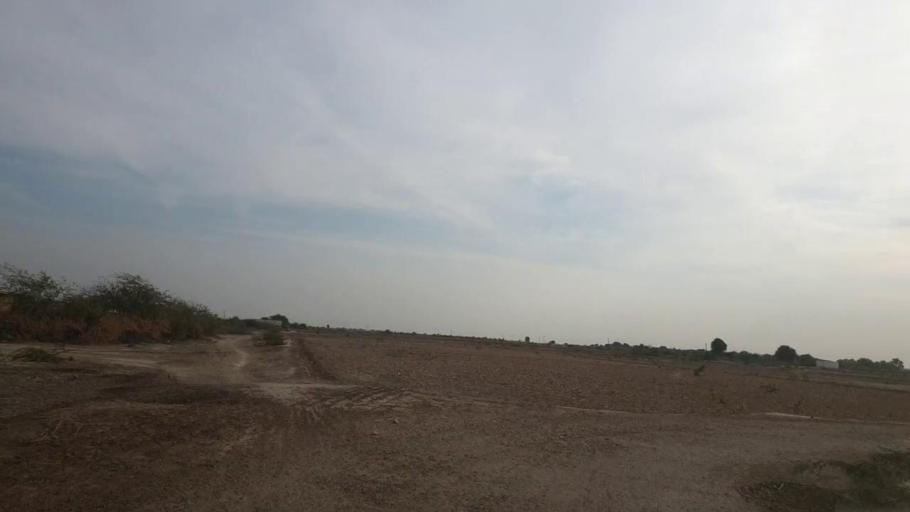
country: PK
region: Sindh
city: Nabisar
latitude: 24.9936
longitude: 69.5182
